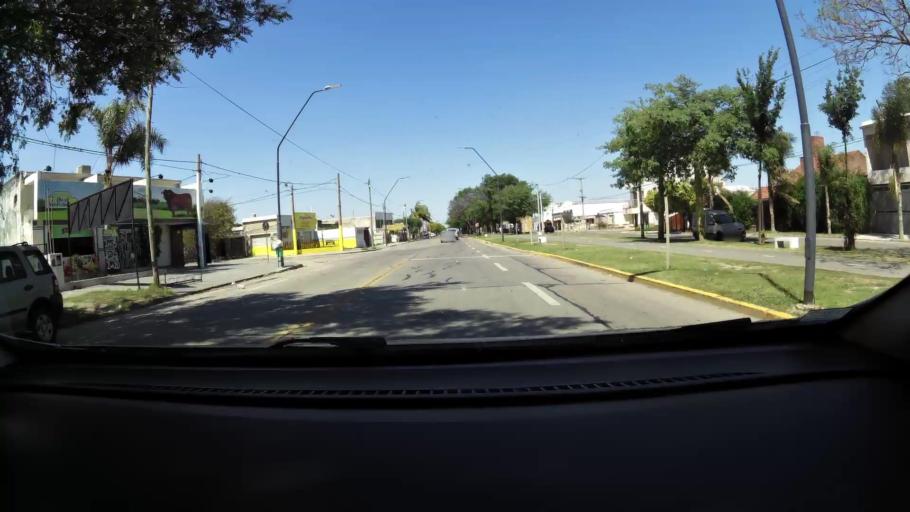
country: AR
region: Cordoba
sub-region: Departamento de Capital
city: Cordoba
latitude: -31.3791
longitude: -64.1418
